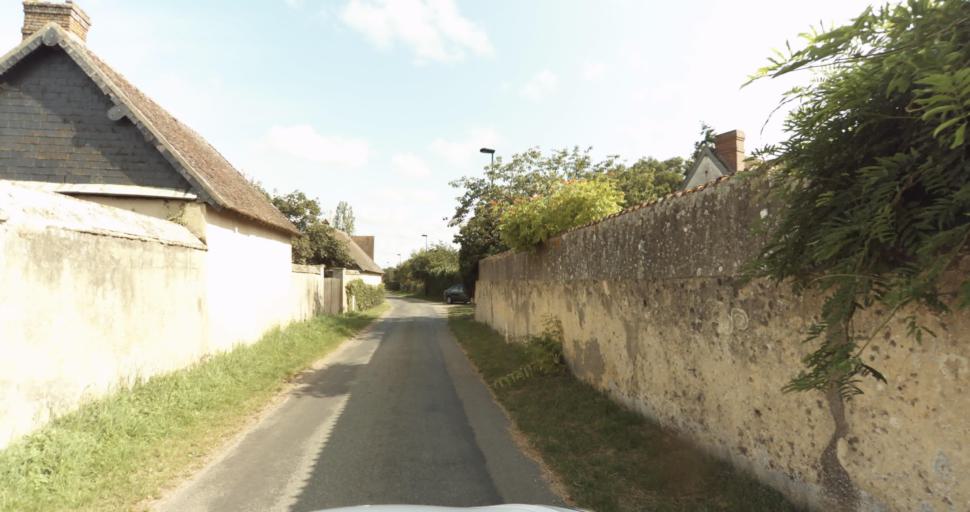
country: FR
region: Haute-Normandie
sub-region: Departement de l'Eure
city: Tillieres-sur-Avre
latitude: 48.7580
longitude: 1.1082
